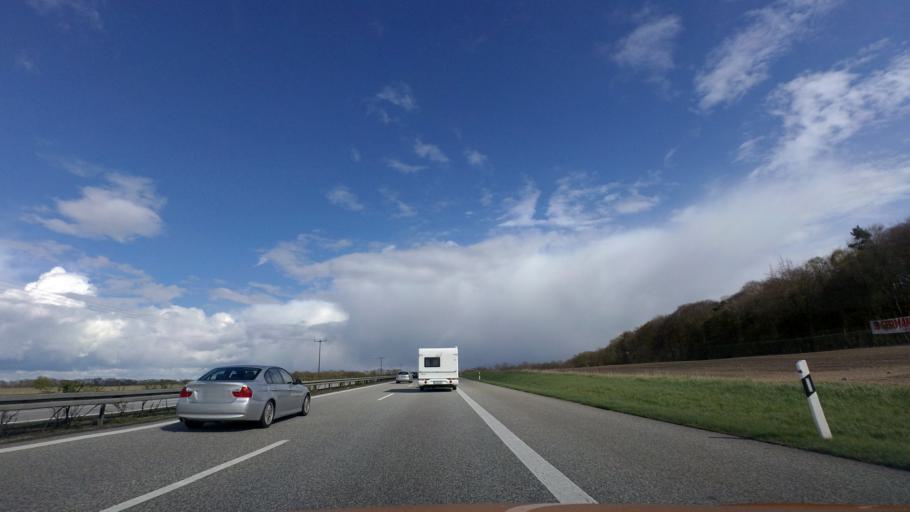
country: DE
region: Mecklenburg-Vorpommern
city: Wittenburg
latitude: 53.5053
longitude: 11.0156
